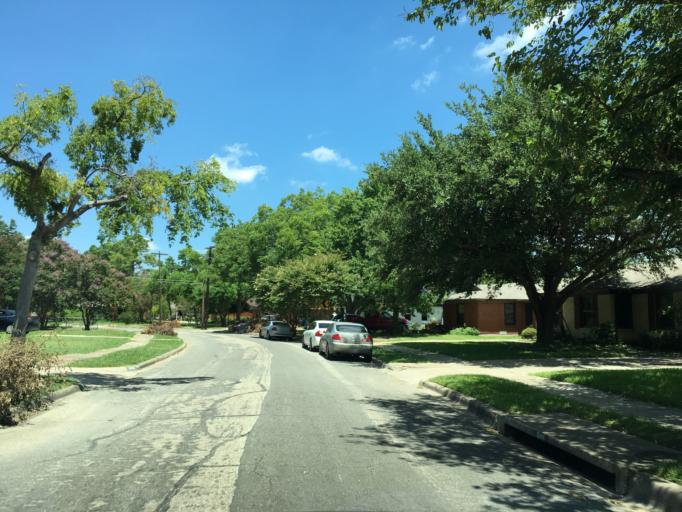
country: US
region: Texas
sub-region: Dallas County
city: Garland
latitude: 32.8368
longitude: -96.6670
